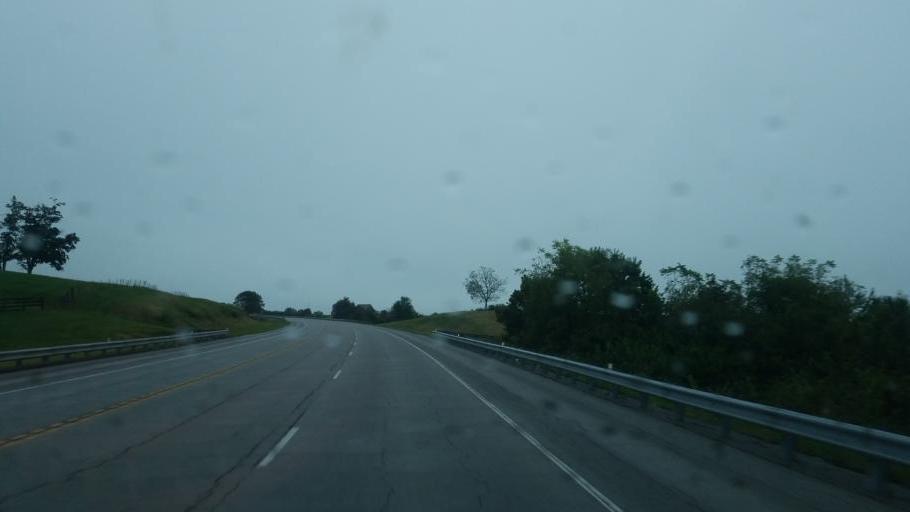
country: US
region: Kentucky
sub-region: Fleming County
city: Flemingsburg
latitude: 38.3967
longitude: -83.7169
